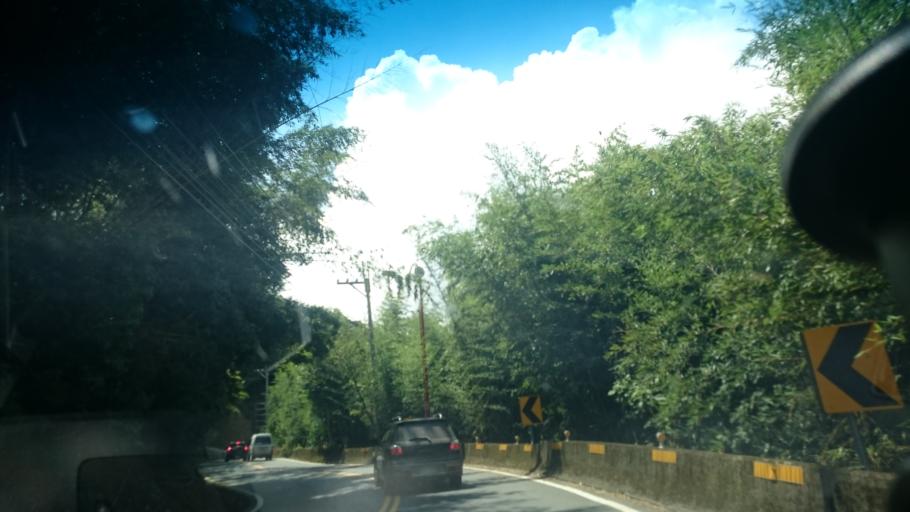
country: TW
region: Taiwan
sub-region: Nantou
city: Puli
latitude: 24.0298
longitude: 121.1446
